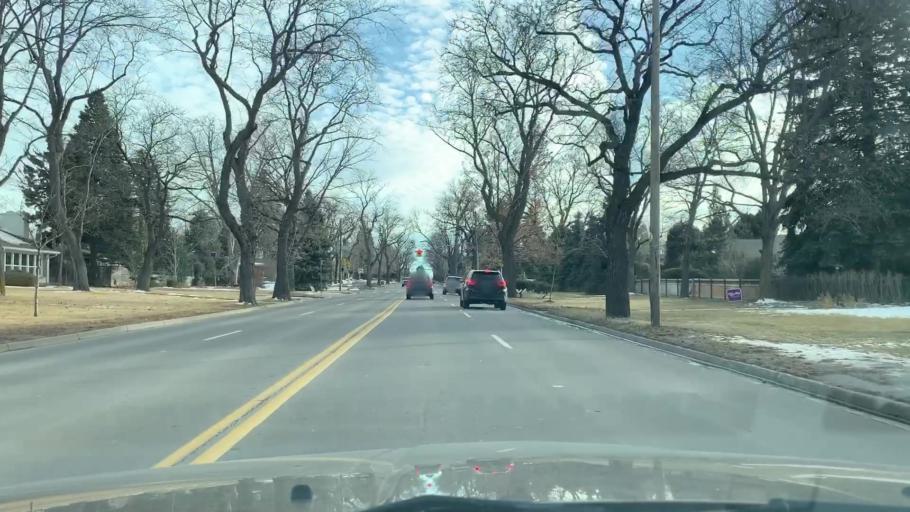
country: US
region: Colorado
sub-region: Arapahoe County
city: Glendale
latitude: 39.7229
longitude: -104.9128
